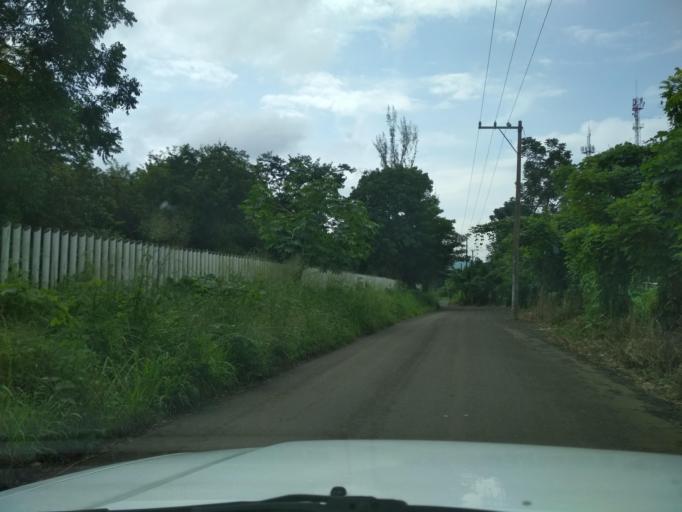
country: MX
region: Veracruz
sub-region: San Andres Tuxtla
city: Matacapan
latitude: 18.4366
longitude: -95.1705
